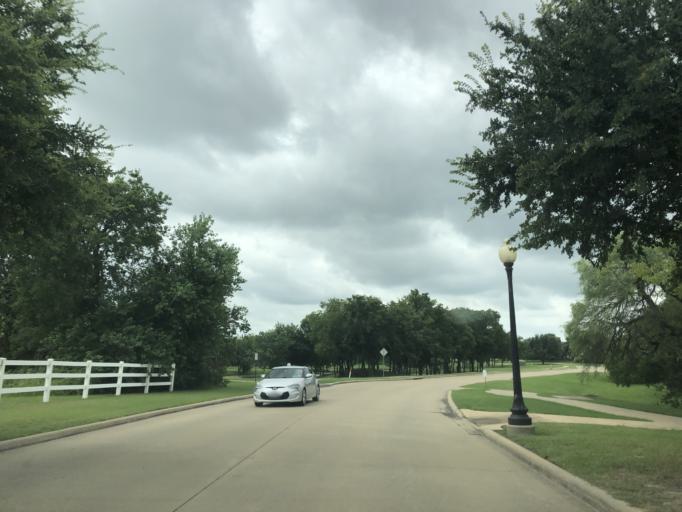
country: US
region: Texas
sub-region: Dallas County
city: Sunnyvale
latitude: 32.8130
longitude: -96.5864
